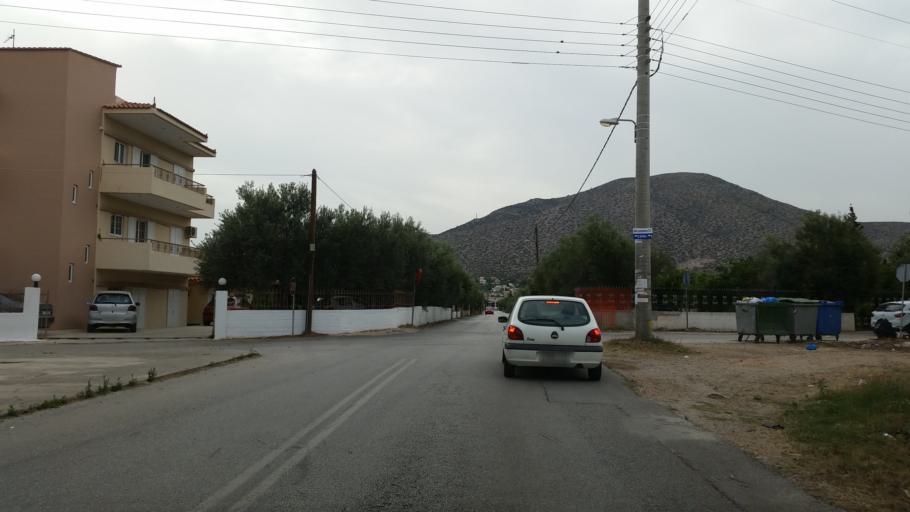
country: GR
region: Attica
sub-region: Nomarchia Anatolikis Attikis
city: Anavyssos
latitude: 37.7349
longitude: 23.9567
